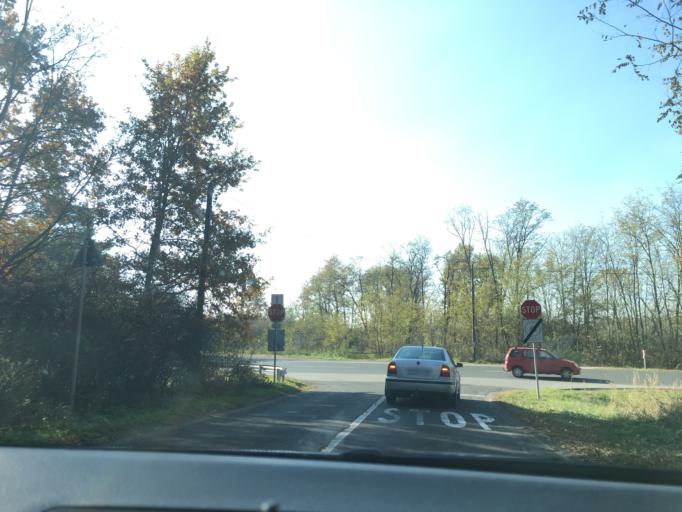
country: HU
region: Hajdu-Bihar
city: Mikepercs
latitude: 47.4848
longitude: 21.7126
